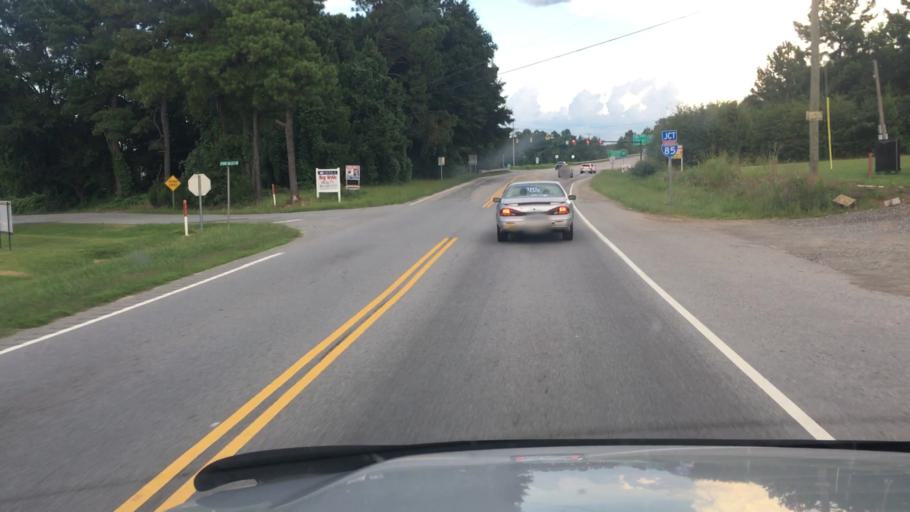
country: US
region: South Carolina
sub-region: Cherokee County
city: Gaffney
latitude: 35.0998
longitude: -81.6738
